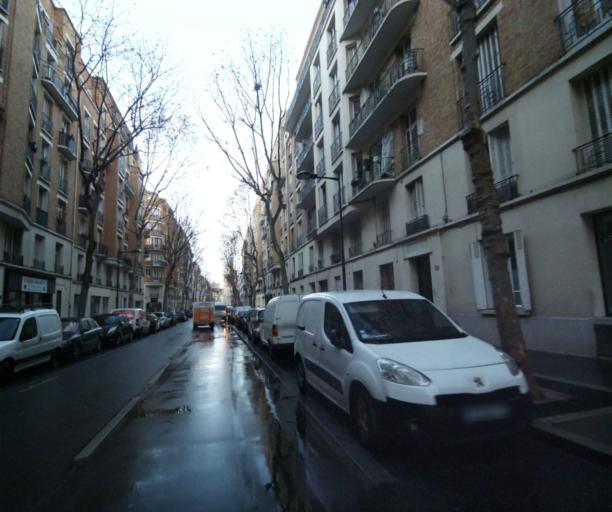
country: FR
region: Ile-de-France
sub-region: Departement des Hauts-de-Seine
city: Clichy
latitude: 48.8973
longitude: 2.3054
